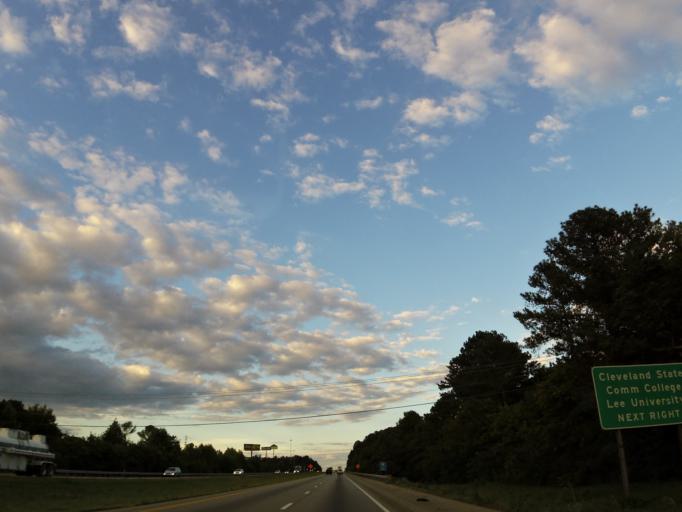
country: US
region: Tennessee
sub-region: Bradley County
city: Cleveland
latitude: 35.1901
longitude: -84.8953
